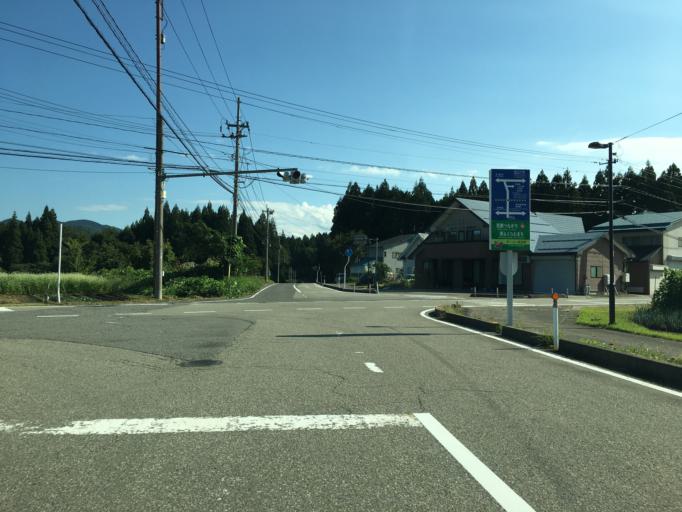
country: JP
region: Fukushima
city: Kitakata
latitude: 37.5972
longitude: 139.6532
